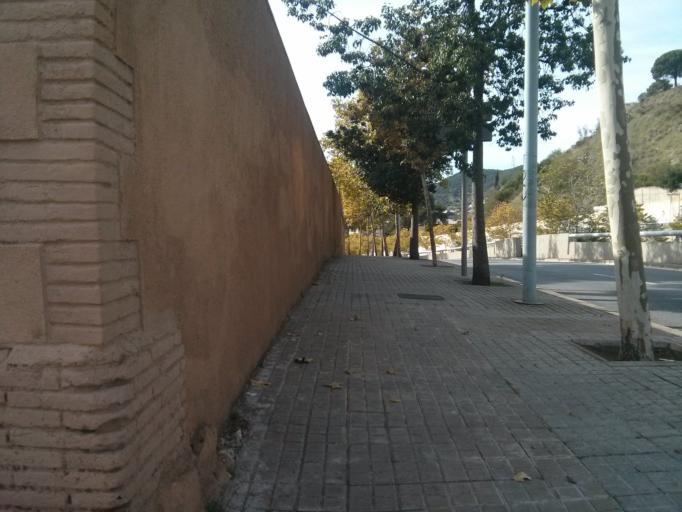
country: ES
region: Catalonia
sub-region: Provincia de Barcelona
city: Sarria-Sant Gervasi
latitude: 41.4086
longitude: 2.1241
